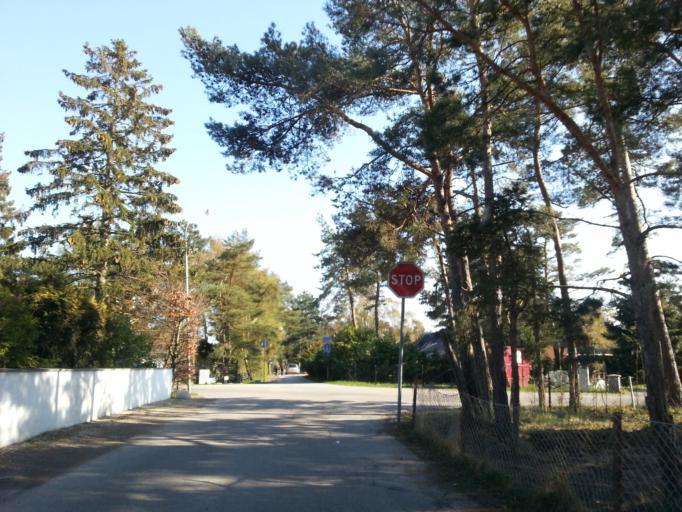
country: SE
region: Skane
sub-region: Vellinge Kommun
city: Hollviken
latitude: 55.4087
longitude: 12.9522
